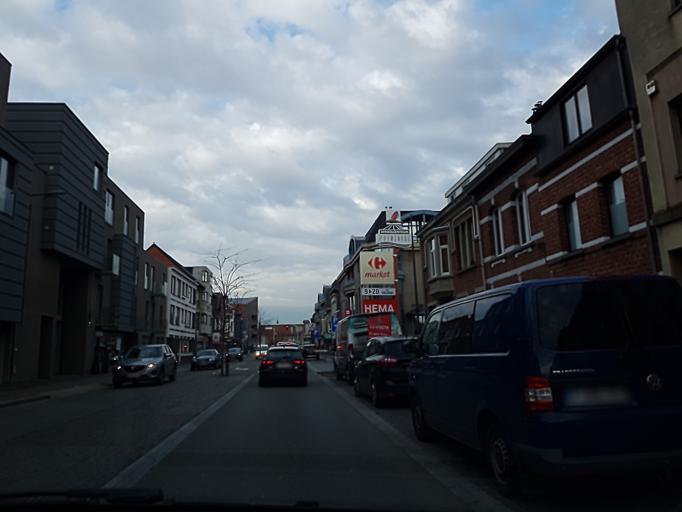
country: BE
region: Flanders
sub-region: Provincie Antwerpen
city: Kapellen
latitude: 51.3121
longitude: 4.4297
